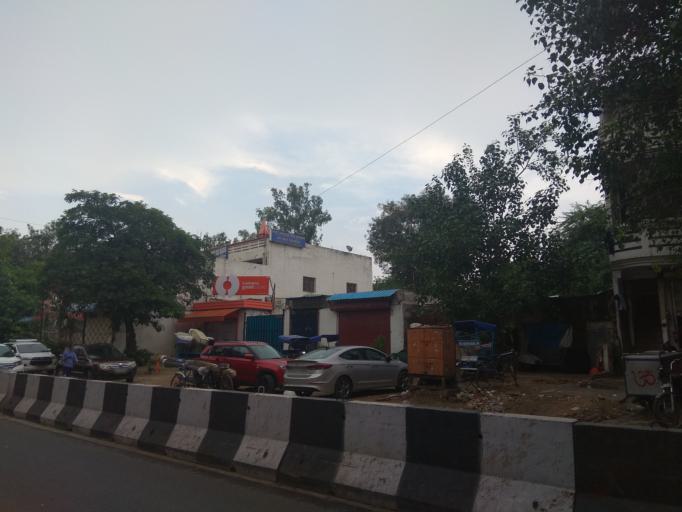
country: IN
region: NCT
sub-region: New Delhi
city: New Delhi
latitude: 28.5699
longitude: 77.2472
